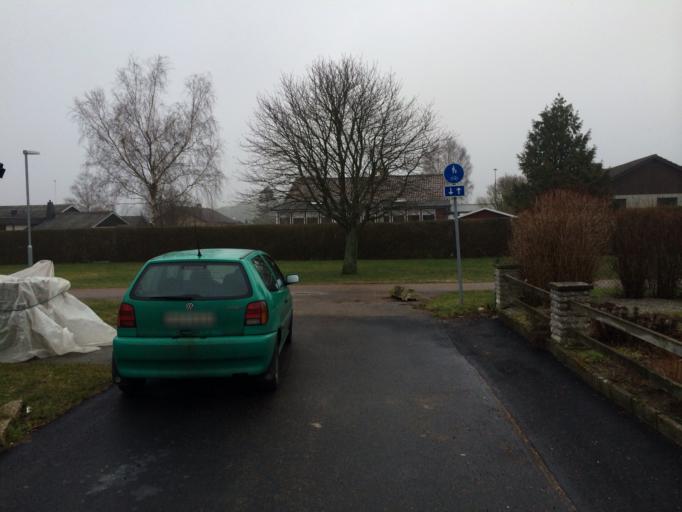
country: SE
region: Skane
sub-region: Landskrona
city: Asmundtorp
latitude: 55.8785
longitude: 12.9959
